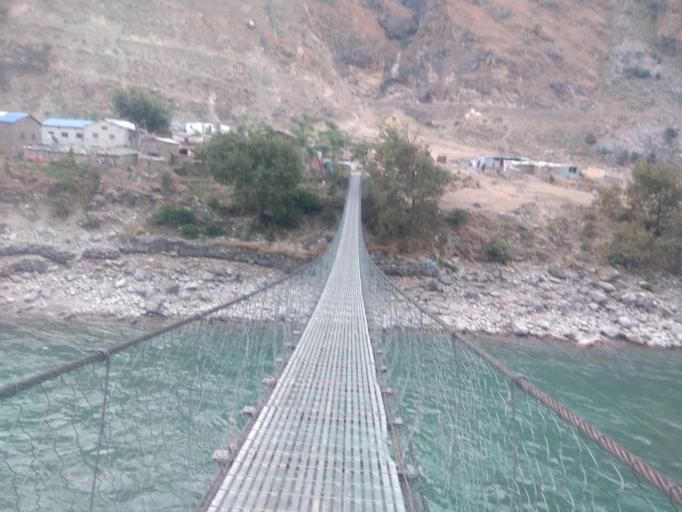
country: NP
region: Mid Western
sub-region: Bheri Zone
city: Dailekh
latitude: 29.2768
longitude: 81.7288
